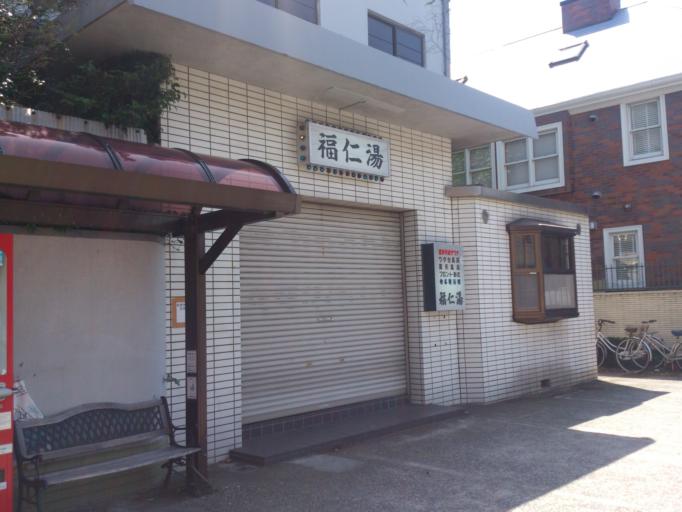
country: JP
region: Chiba
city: Chiba
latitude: 35.6560
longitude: 140.0583
